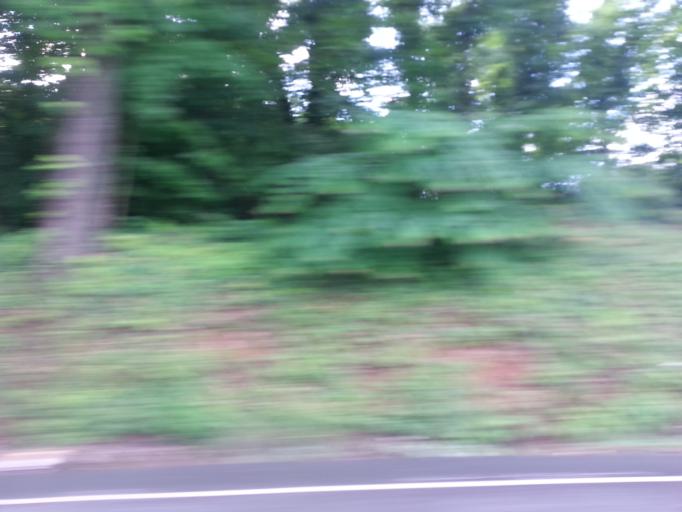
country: US
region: Tennessee
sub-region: Knox County
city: Knoxville
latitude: 35.9316
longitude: -83.9886
